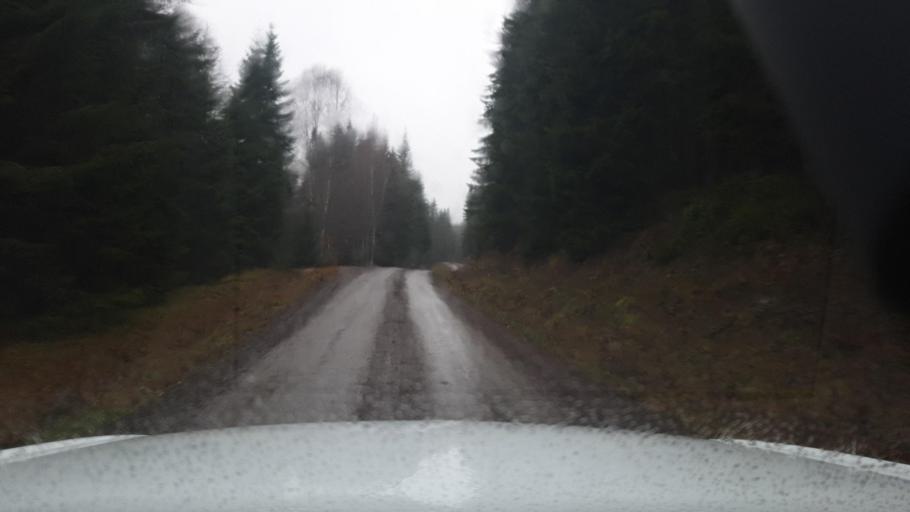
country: SE
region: Vaermland
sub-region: Sunne Kommun
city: Sunne
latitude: 59.8608
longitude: 12.8783
